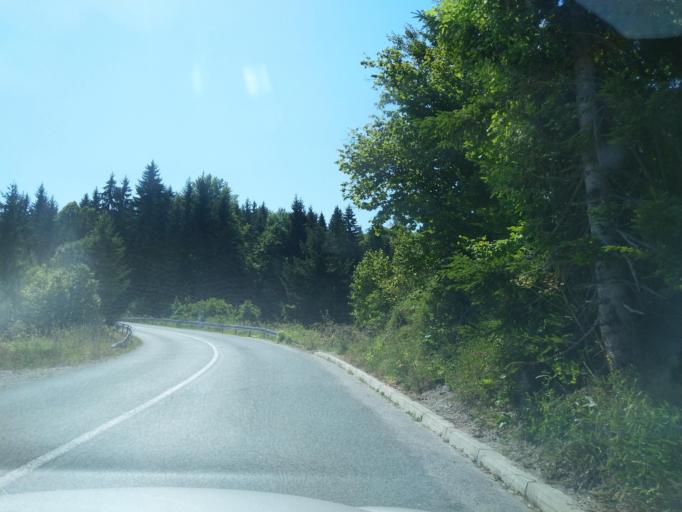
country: RS
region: Central Serbia
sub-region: Zlatiborski Okrug
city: Nova Varos
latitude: 43.4077
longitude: 19.8399
